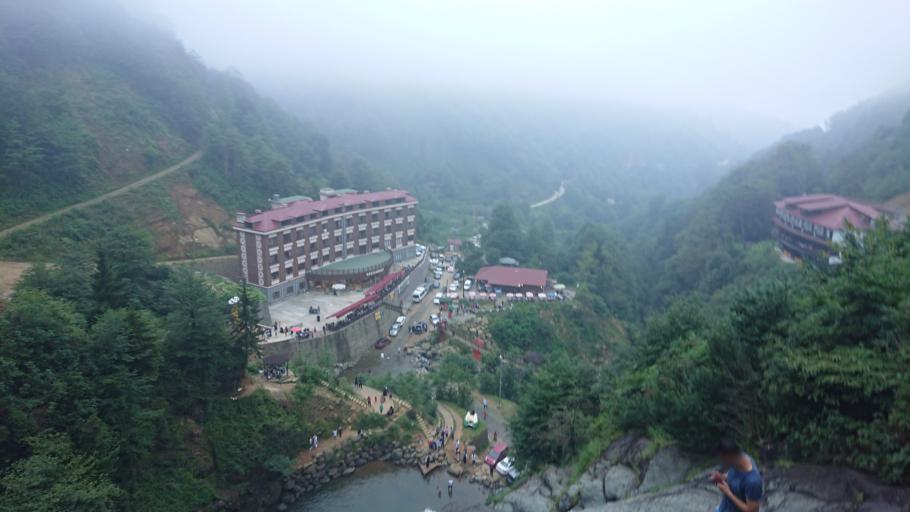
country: TR
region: Rize
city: Hemsin
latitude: 41.0451
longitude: 40.8092
